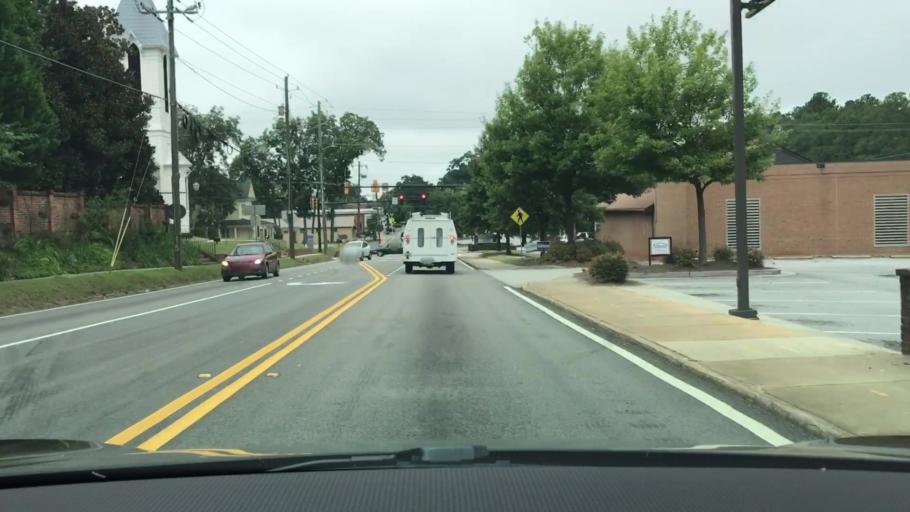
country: US
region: Georgia
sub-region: Oconee County
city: Watkinsville
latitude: 33.8616
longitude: -83.4079
